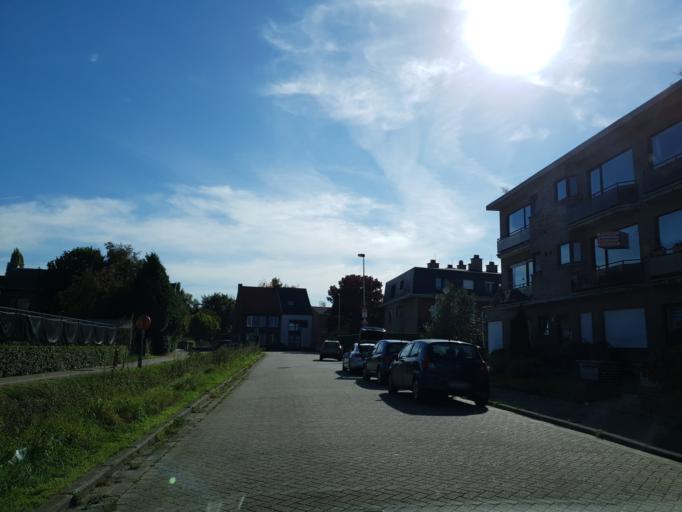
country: BE
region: Flanders
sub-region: Provincie Antwerpen
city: Kapellen
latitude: 51.3001
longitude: 4.4208
